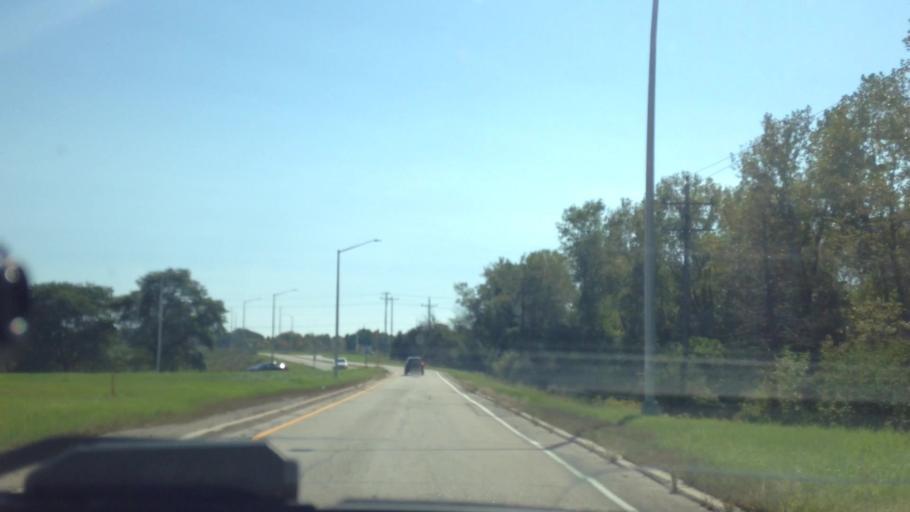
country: US
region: Wisconsin
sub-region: Milwaukee County
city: River Hills
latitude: 43.1792
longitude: -87.9188
